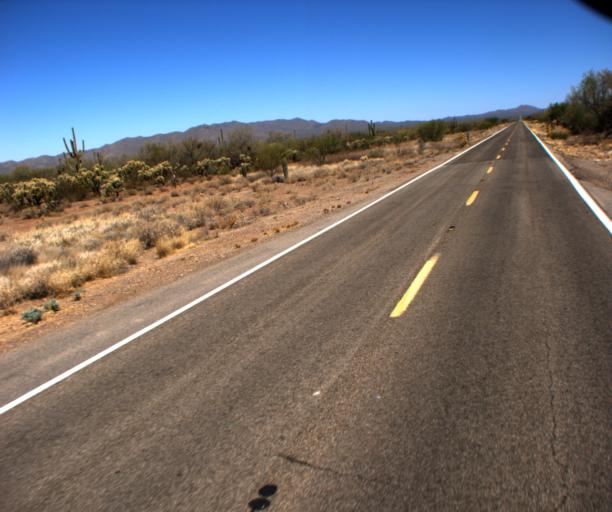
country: US
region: Arizona
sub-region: Pima County
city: Sells
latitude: 32.0627
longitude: -112.0354
